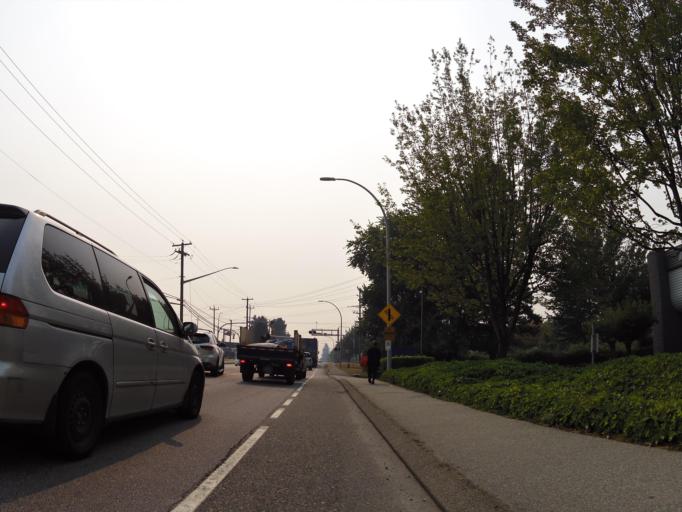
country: CA
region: British Columbia
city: Surrey
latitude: 49.1419
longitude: -122.8568
